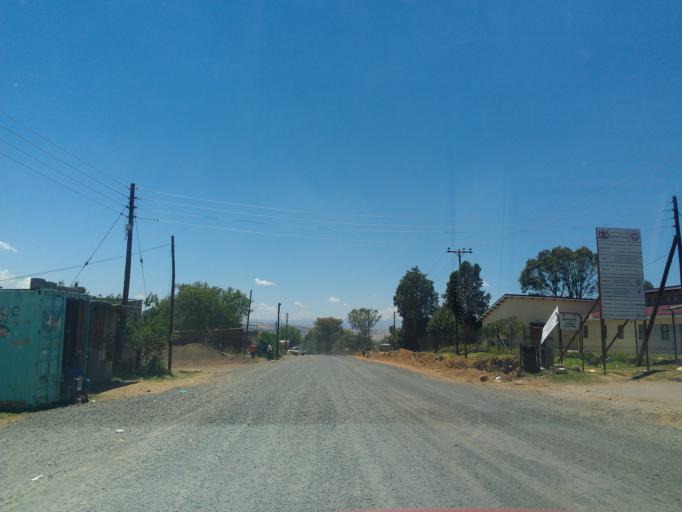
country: LS
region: Berea
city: Teyateyaneng
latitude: -29.1479
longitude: 27.7531
